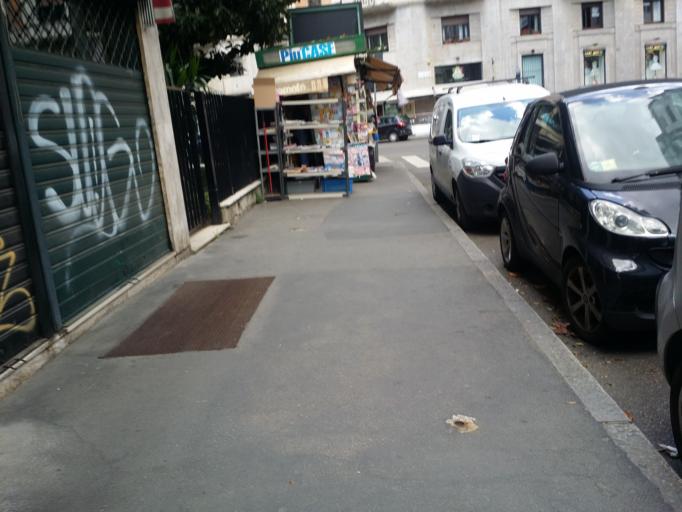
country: IT
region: Lombardy
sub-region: Citta metropolitana di Milano
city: Milano
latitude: 45.4658
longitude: 9.1620
